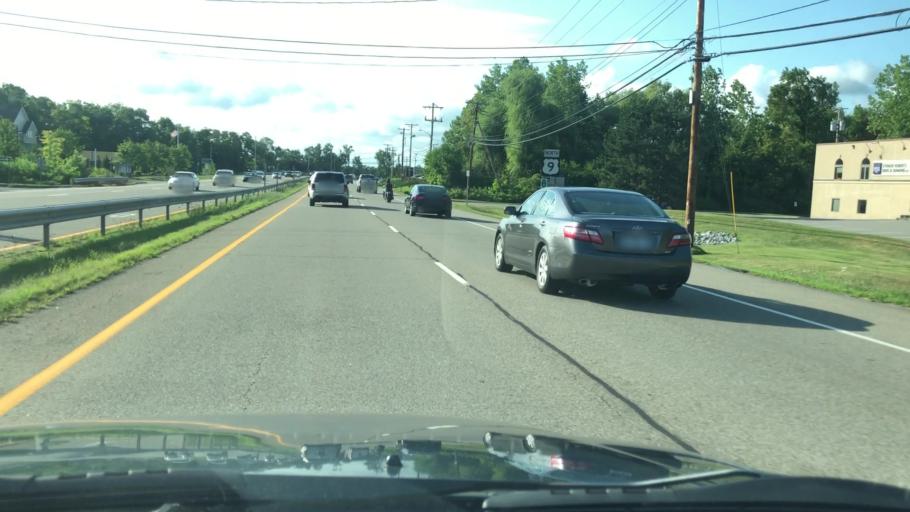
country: US
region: New York
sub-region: Dutchess County
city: Fishkill
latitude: 41.5650
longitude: -73.9058
